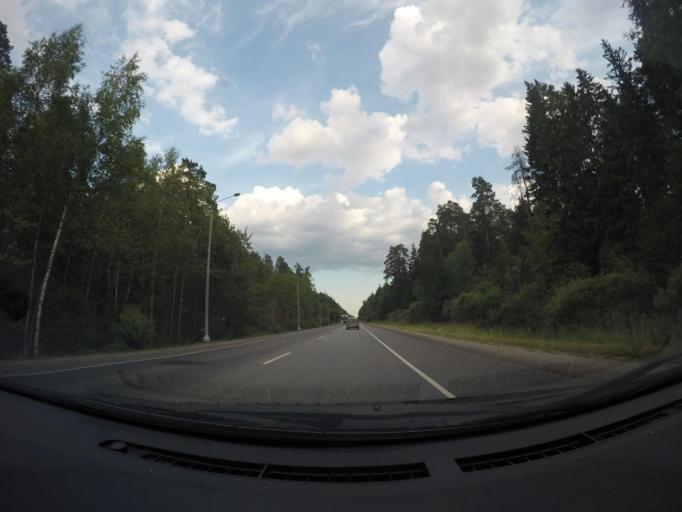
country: RU
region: Moskovskaya
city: Yegor'yevsk
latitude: 55.4552
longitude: 38.9947
